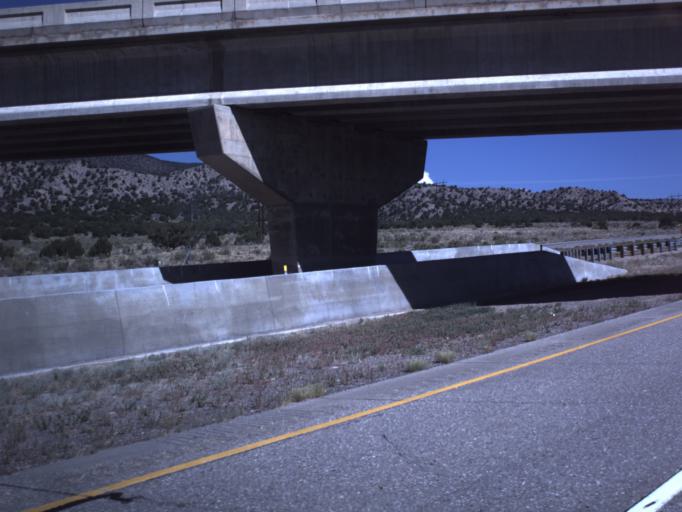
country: US
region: Utah
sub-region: Sevier County
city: Monroe
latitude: 38.5898
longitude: -112.2701
